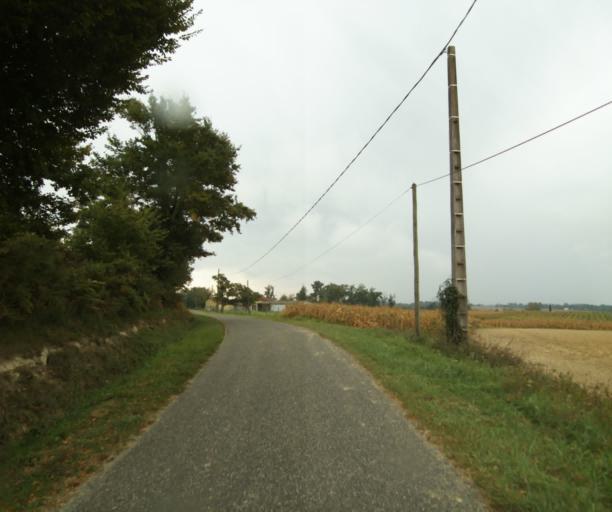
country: FR
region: Midi-Pyrenees
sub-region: Departement du Gers
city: Cazaubon
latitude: 43.9222
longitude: -0.1870
